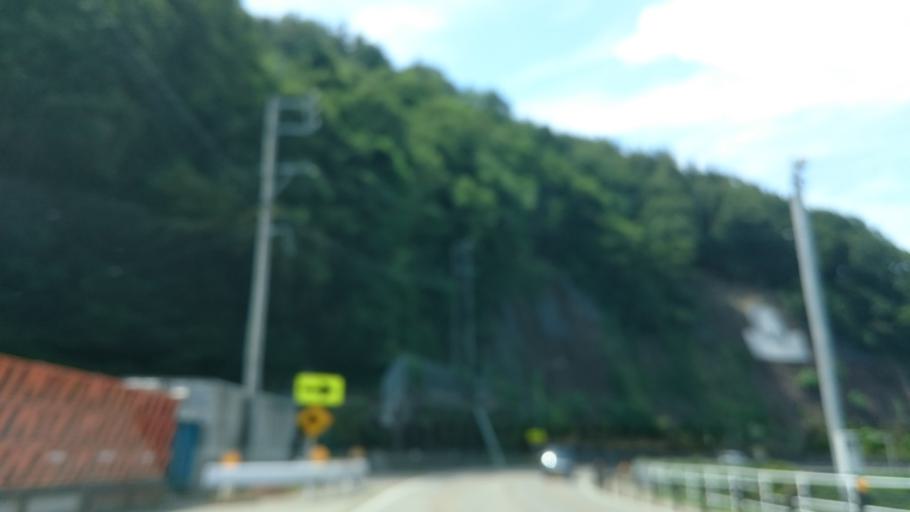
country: JP
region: Gifu
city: Takayama
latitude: 36.1040
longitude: 137.2623
